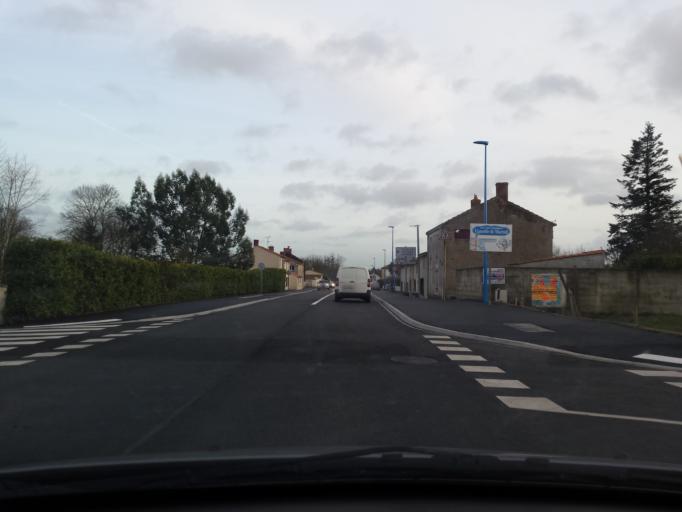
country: FR
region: Pays de la Loire
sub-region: Departement de la Vendee
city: Saint-Florent-des-Bois
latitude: 46.5737
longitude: -1.2850
